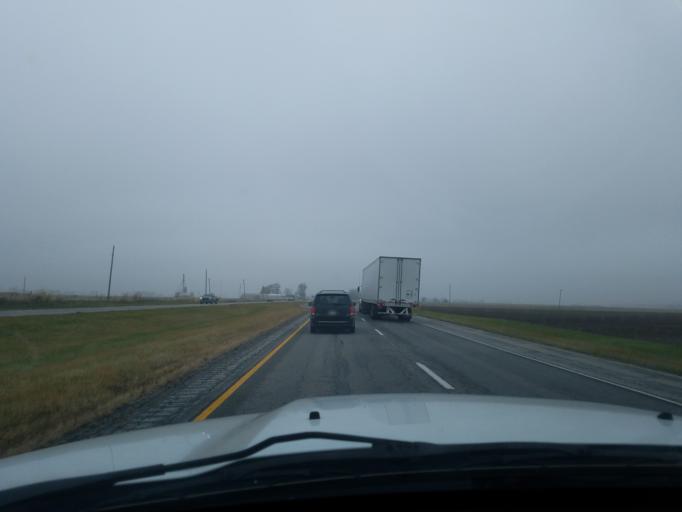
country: US
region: Indiana
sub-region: Howard County
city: Indian Heights
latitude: 40.3308
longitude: -86.1268
